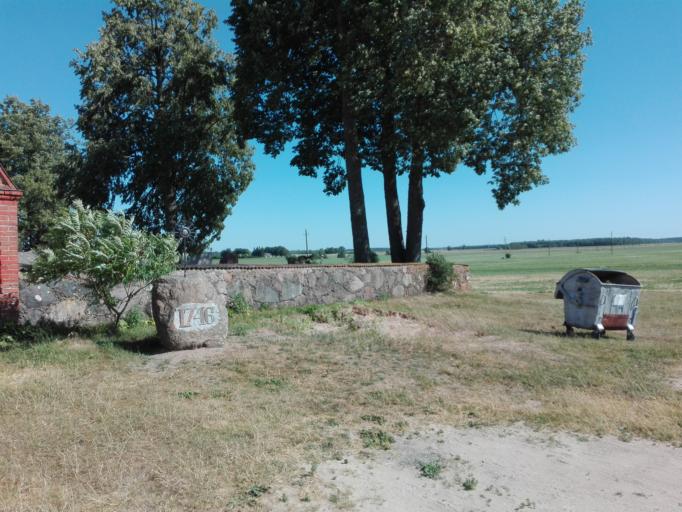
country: LT
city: Vabalninkas
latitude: 56.0215
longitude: 24.6424
